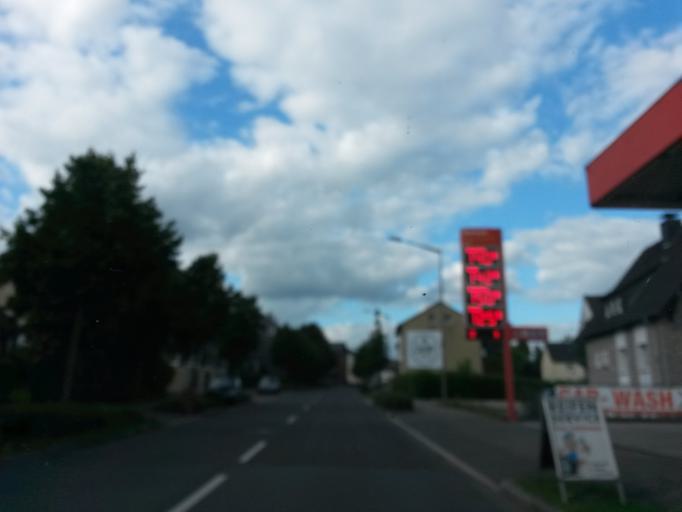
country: DE
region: North Rhine-Westphalia
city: Bergneustadt
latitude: 51.0173
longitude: 7.6397
